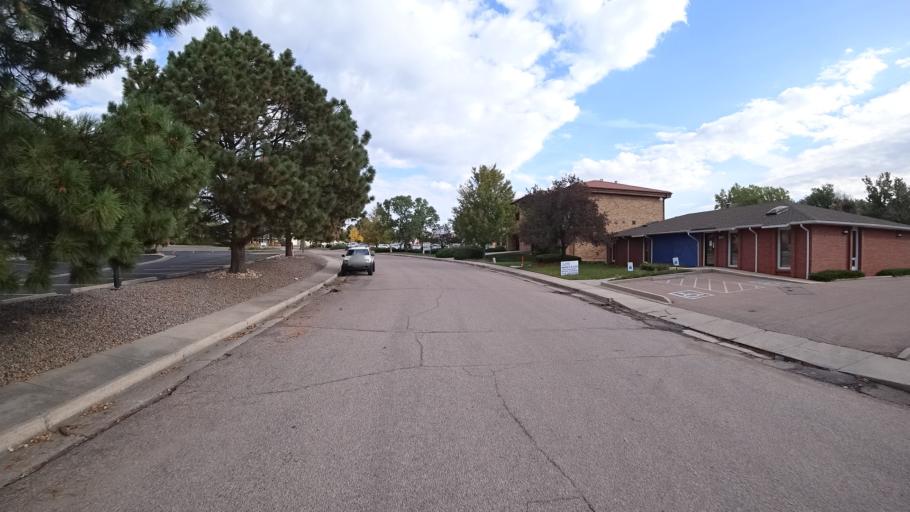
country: US
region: Colorado
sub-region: El Paso County
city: Cimarron Hills
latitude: 38.8635
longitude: -104.7550
